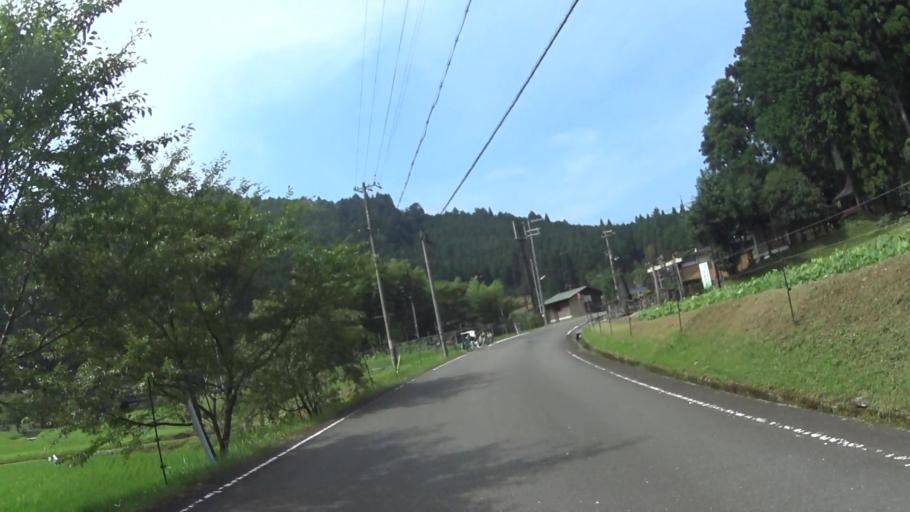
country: JP
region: Fukui
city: Obama
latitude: 35.3205
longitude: 135.6425
